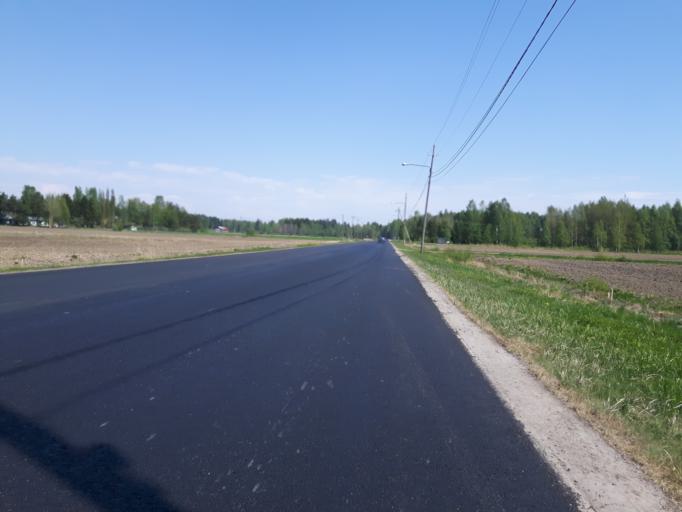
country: FI
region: Uusimaa
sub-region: Helsinki
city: Pornainen
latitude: 60.3314
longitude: 25.4479
